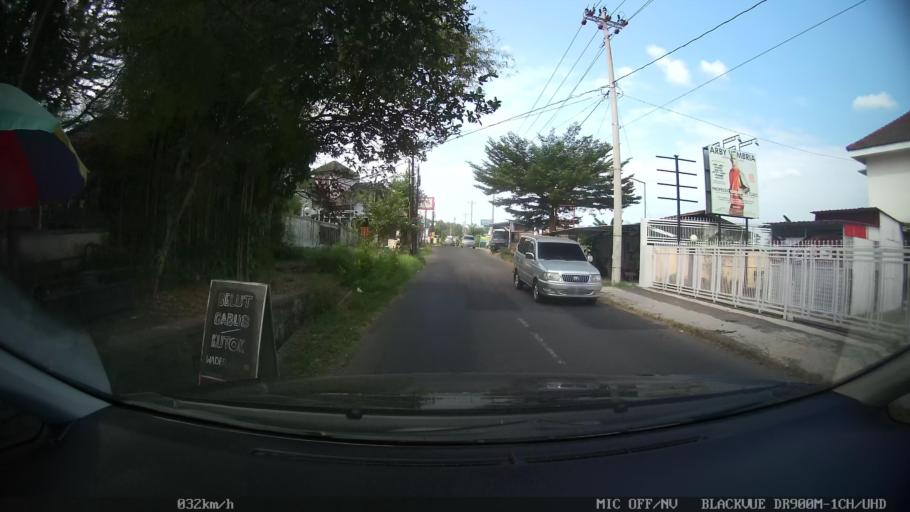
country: ID
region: Daerah Istimewa Yogyakarta
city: Depok
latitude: -7.7301
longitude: 110.4072
